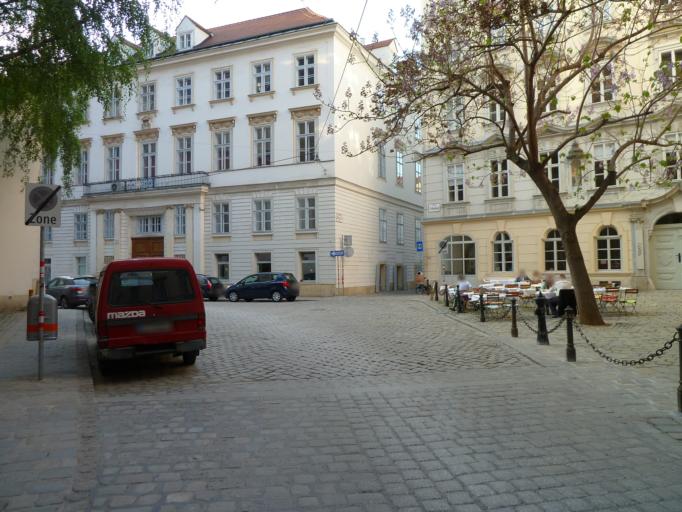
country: AT
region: Vienna
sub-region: Wien Stadt
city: Vienna
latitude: 48.2108
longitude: 16.3692
